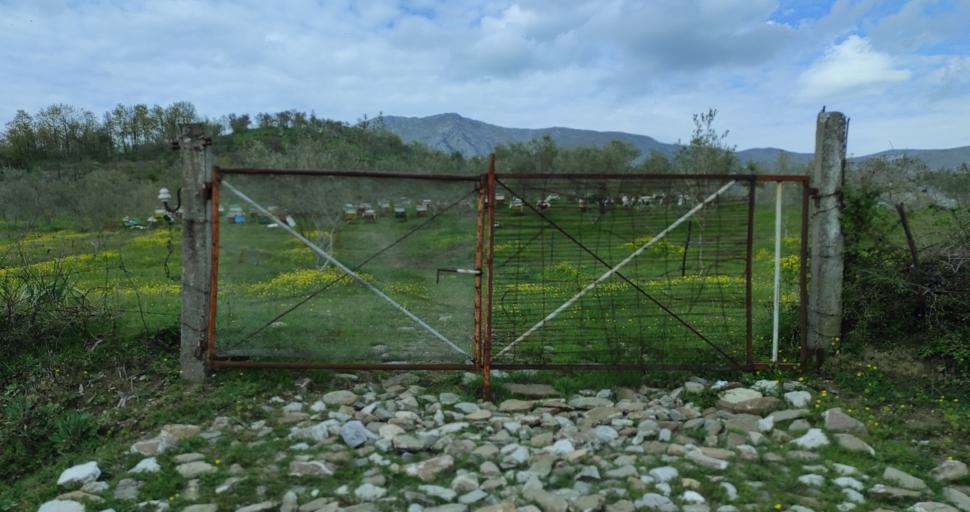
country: AL
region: Shkoder
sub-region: Rrethi i Shkodres
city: Dajc
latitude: 42.0345
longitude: 19.4056
